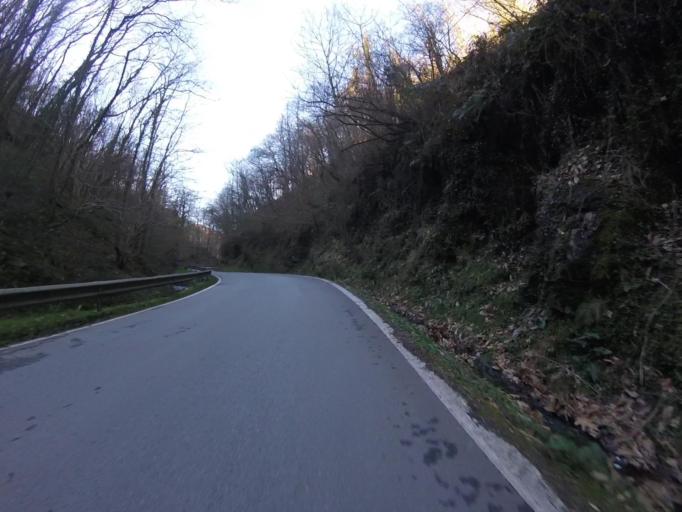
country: ES
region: Navarre
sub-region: Provincia de Navarra
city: Lesaka
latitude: 43.2513
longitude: -1.7214
